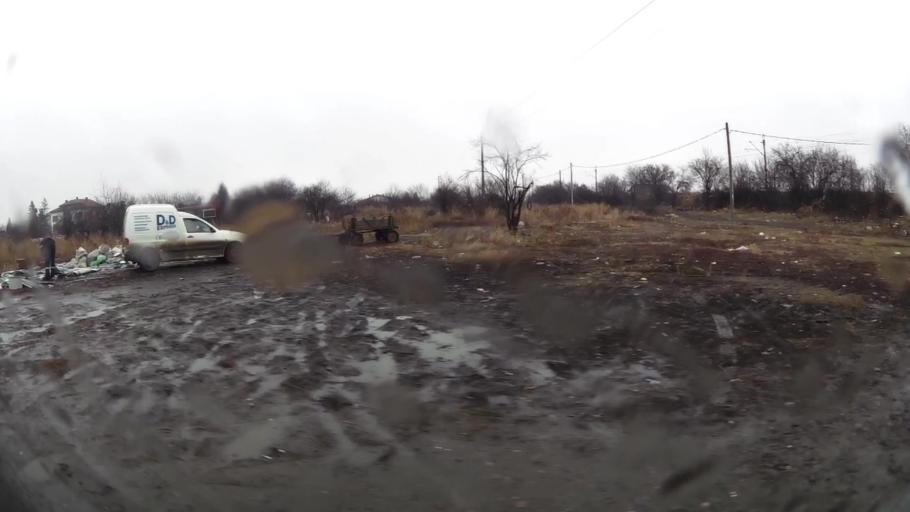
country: BG
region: Sofia-Capital
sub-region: Stolichna Obshtina
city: Sofia
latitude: 42.6618
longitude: 23.4276
